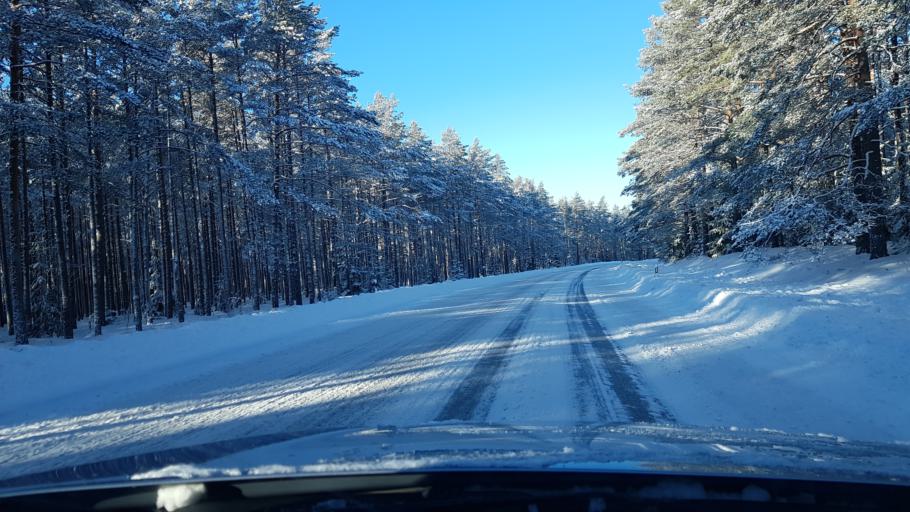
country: EE
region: Hiiumaa
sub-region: Kaerdla linn
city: Kardla
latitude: 58.9272
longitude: 22.7863
